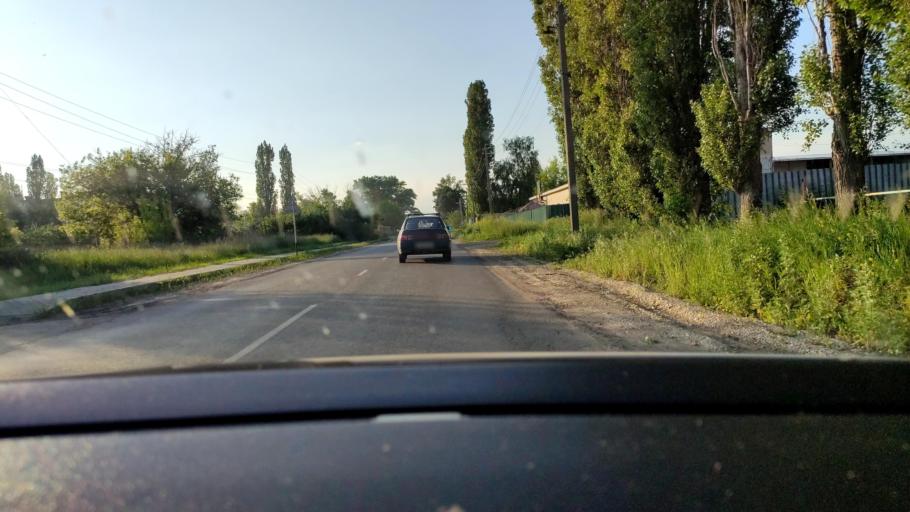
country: RU
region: Voronezj
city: Maslovka
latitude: 51.5373
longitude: 39.3428
